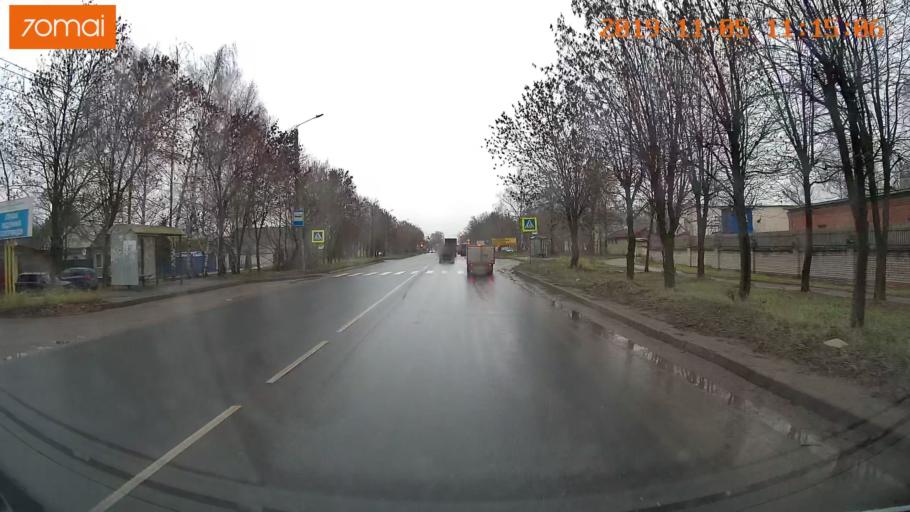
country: RU
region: Ivanovo
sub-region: Gorod Ivanovo
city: Ivanovo
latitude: 56.9762
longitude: 40.9543
